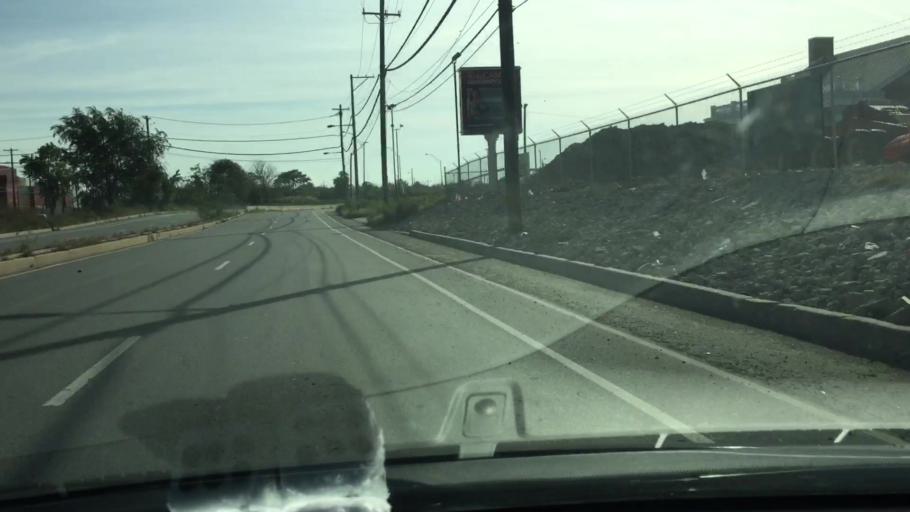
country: US
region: New Jersey
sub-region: Camden County
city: Gloucester City
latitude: 39.9057
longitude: -75.1398
